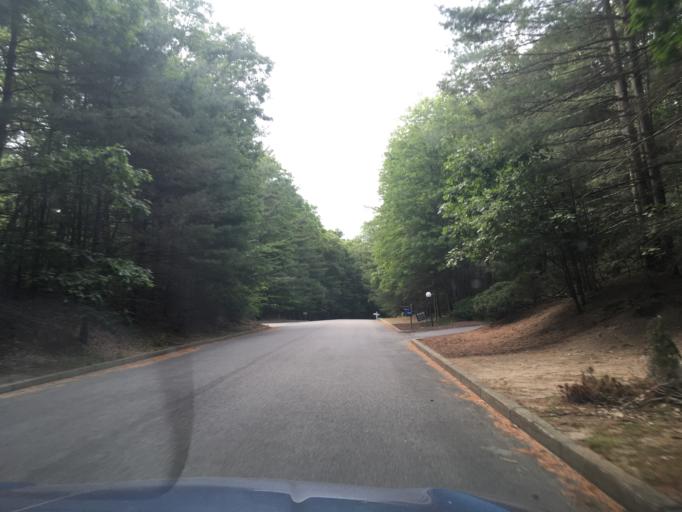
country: US
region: Rhode Island
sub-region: Washington County
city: Exeter
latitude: 41.6304
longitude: -71.5378
